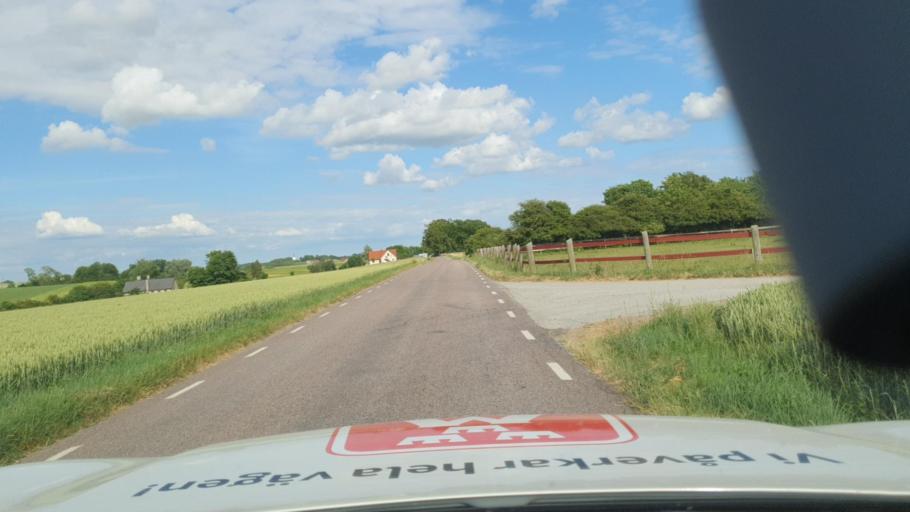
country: SE
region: Skane
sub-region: Skurups Kommun
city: Skurup
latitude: 55.4486
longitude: 13.4886
